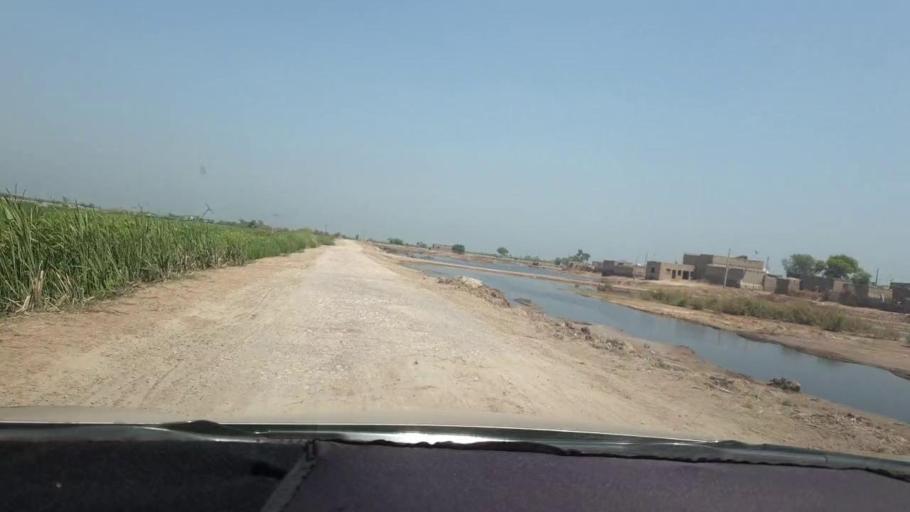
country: PK
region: Sindh
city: Shahdadkot
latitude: 27.8392
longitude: 68.0016
